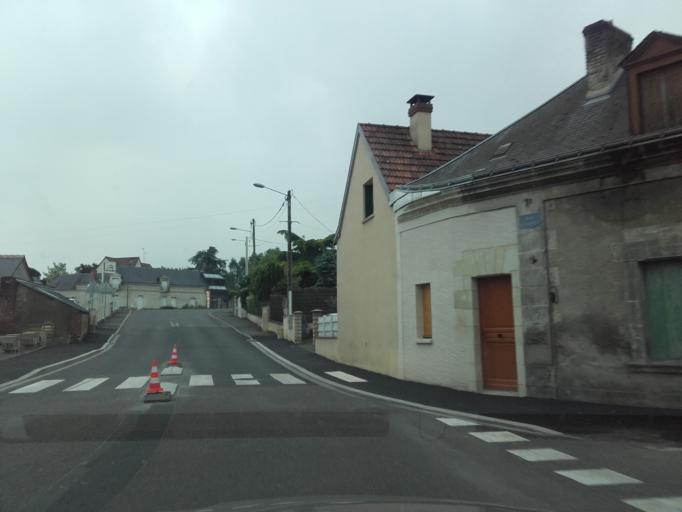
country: FR
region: Centre
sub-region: Departement d'Indre-et-Loire
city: Cerelles
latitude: 47.4926
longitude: 0.6966
